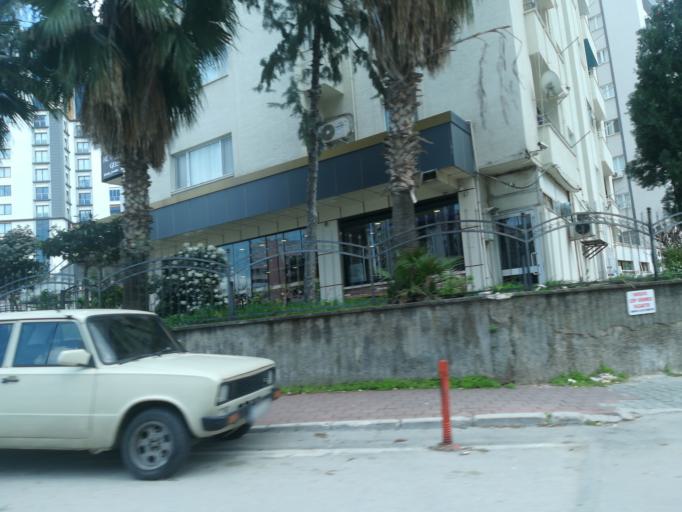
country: TR
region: Adana
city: Adana
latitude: 37.0411
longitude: 35.3135
